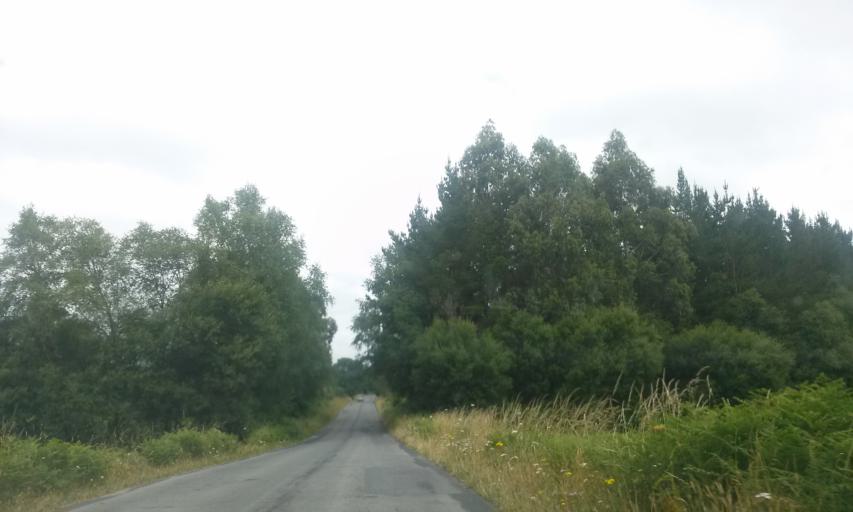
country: ES
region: Galicia
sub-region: Provincia de Lugo
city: Friol
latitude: 43.0945
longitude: -7.8090
